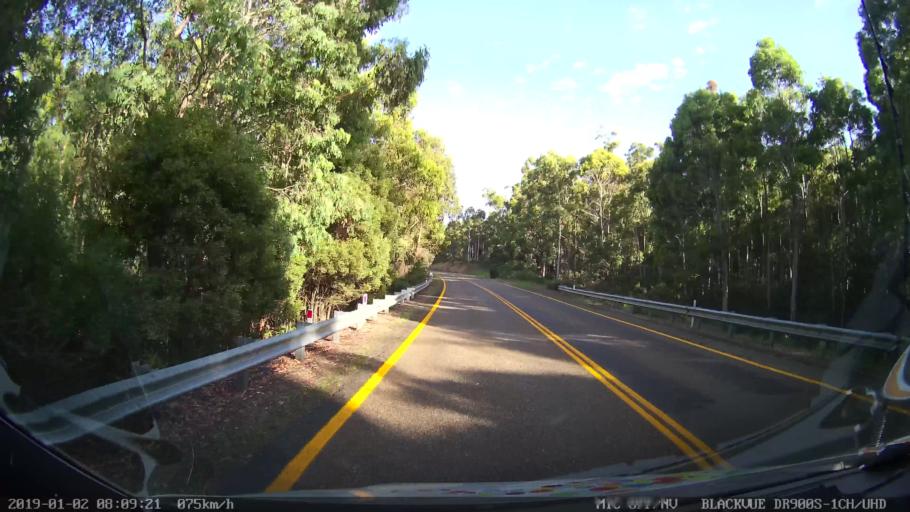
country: AU
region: New South Wales
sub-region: Tumut Shire
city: Tumut
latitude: -35.6076
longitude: 148.3803
